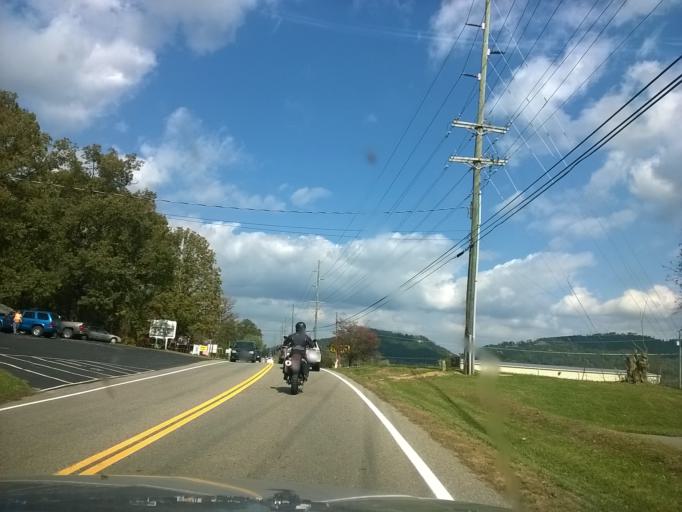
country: US
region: Tennessee
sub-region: Sevier County
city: Pigeon Forge
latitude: 35.7282
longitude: -83.6335
